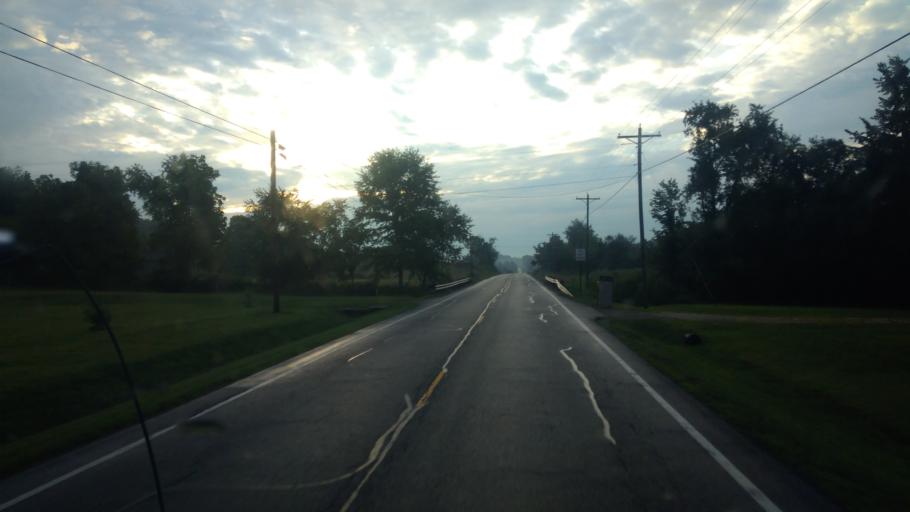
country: US
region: Ohio
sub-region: Guernsey County
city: Byesville
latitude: 39.9848
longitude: -81.3956
